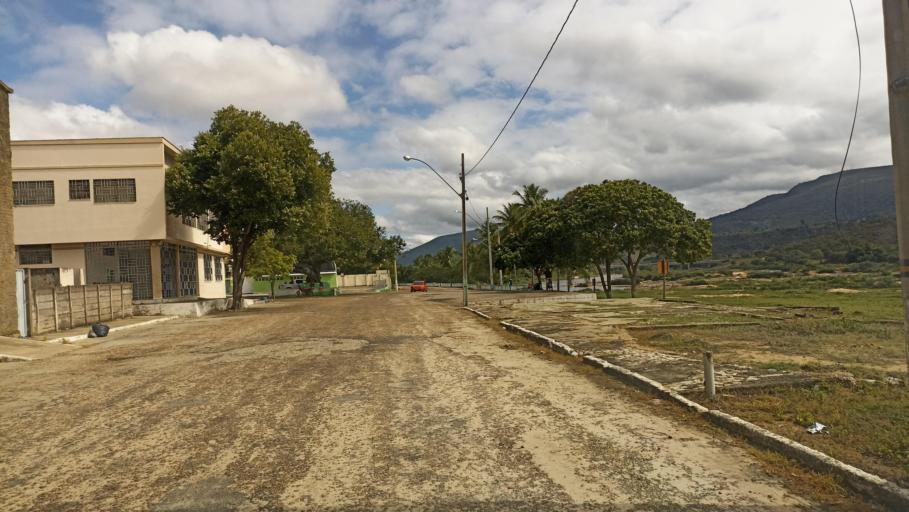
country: BR
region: Minas Gerais
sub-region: Jequitinhonha
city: Jequitinhonha
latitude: -16.4320
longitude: -41.0029
